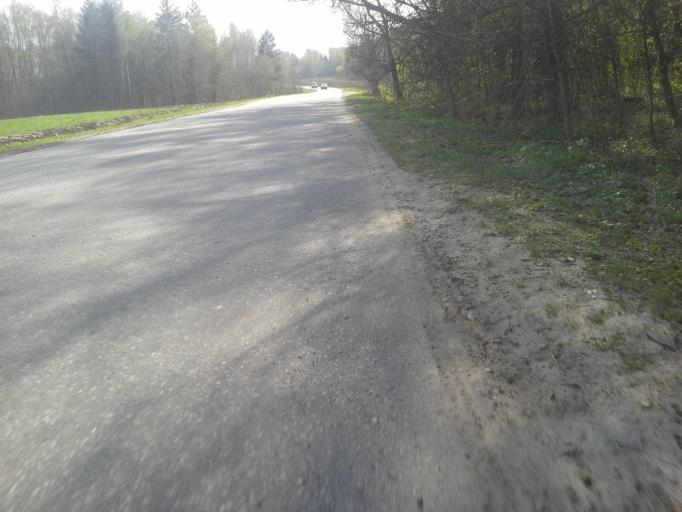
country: RU
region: Moskovskaya
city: Dubrovitsy
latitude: 55.4335
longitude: 37.4389
